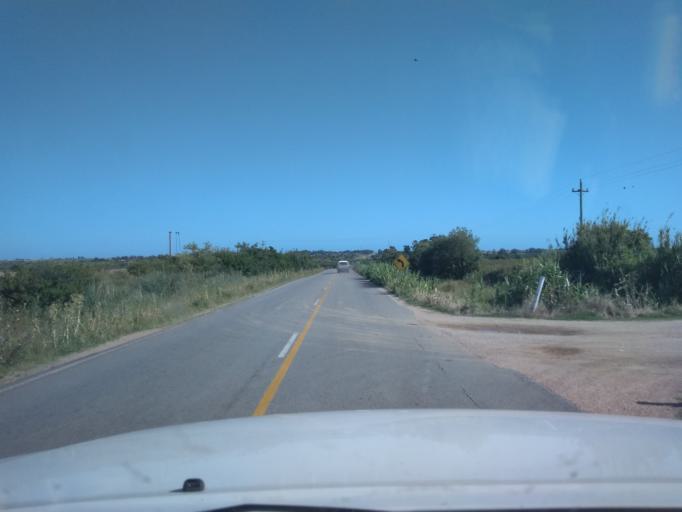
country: UY
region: Canelones
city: San Ramon
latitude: -34.3348
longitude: -55.9599
